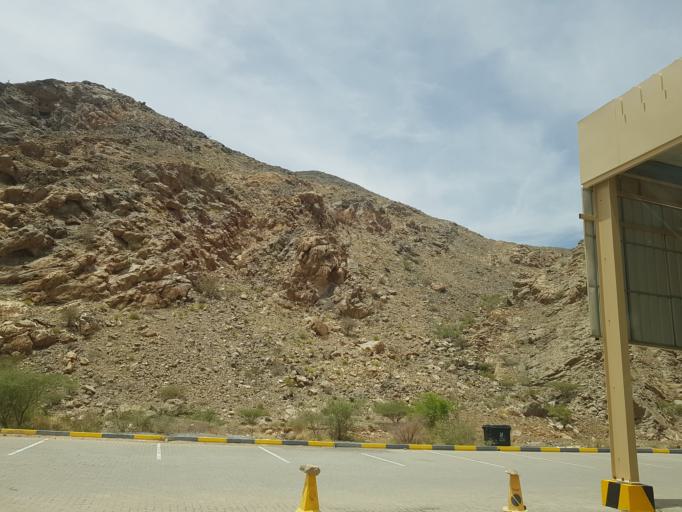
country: OM
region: Muhafazat ad Dakhiliyah
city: Izki
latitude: 22.9607
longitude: 57.6779
